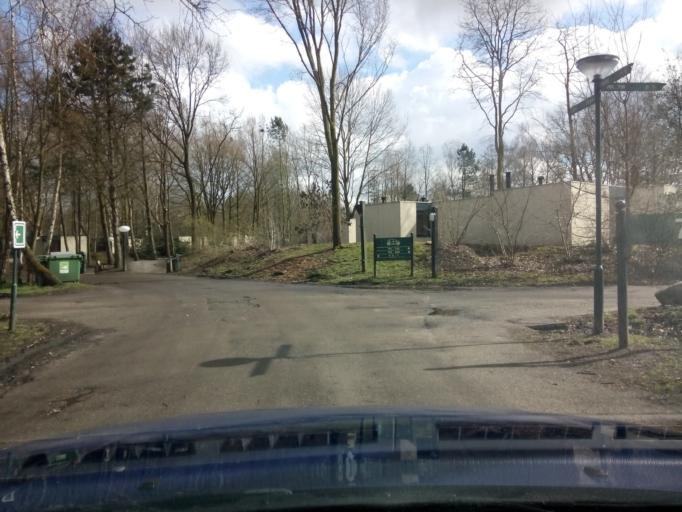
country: NL
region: Drenthe
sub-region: Gemeente Coevorden
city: Dalen
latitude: 52.6785
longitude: 6.7697
